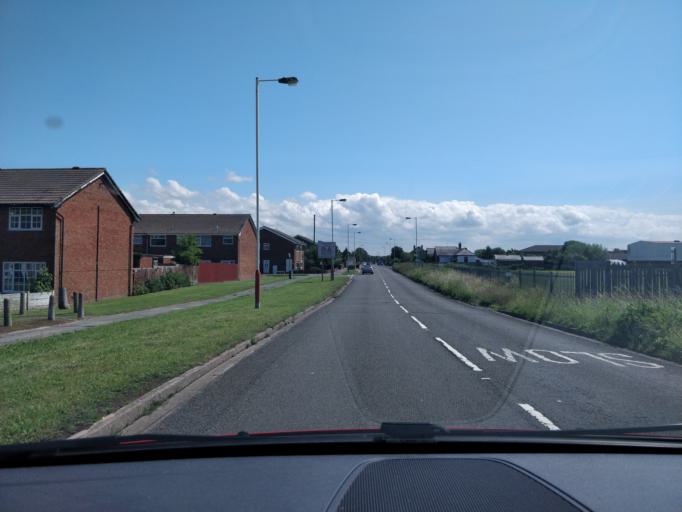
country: GB
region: England
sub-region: Sefton
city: Southport
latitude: 53.6724
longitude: -2.9755
